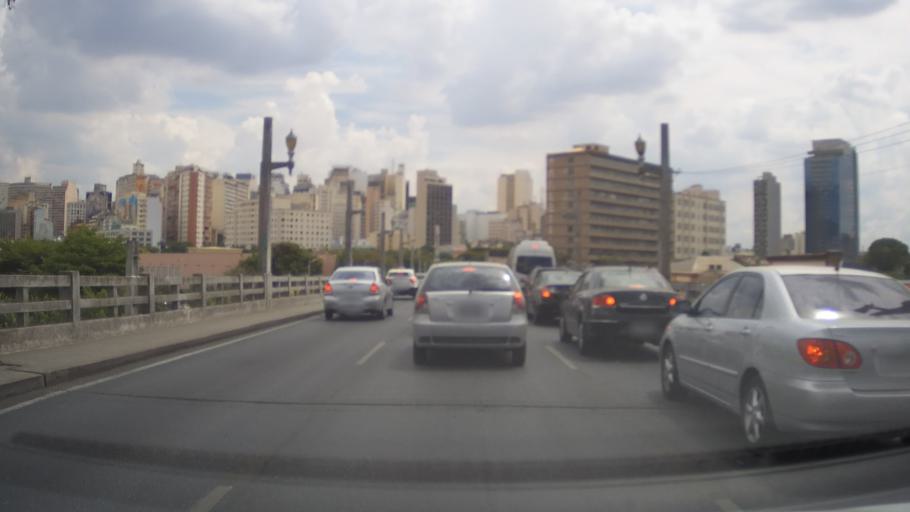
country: BR
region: Minas Gerais
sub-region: Belo Horizonte
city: Belo Horizonte
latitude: -19.9141
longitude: -43.9325
